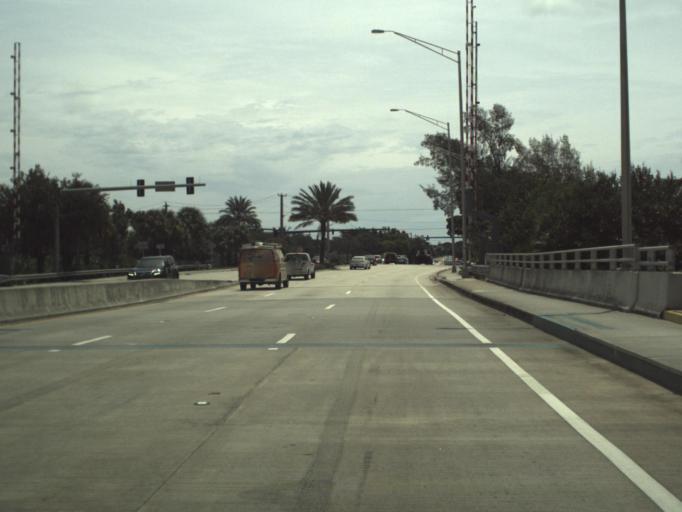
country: US
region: Florida
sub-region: Palm Beach County
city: North Palm Beach
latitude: 26.8445
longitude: -80.0664
